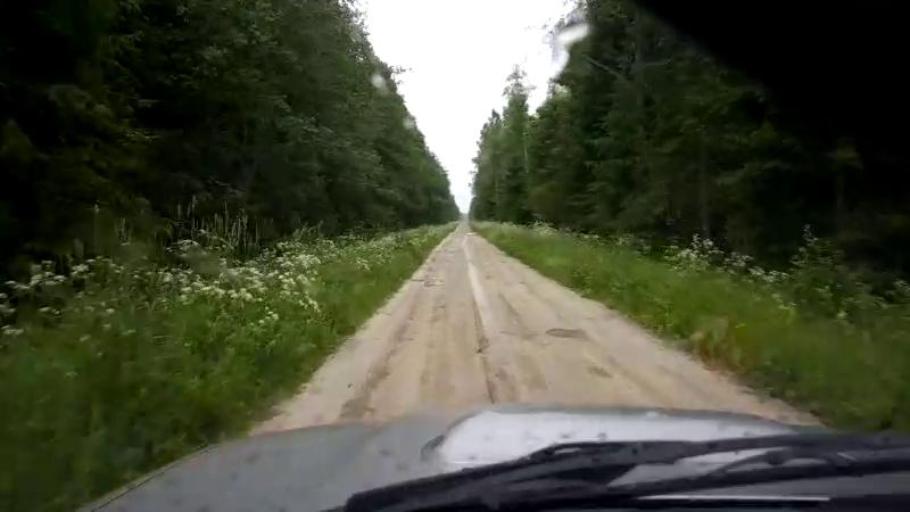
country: EE
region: Paernumaa
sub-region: Halinga vald
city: Parnu-Jaagupi
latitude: 58.5834
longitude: 24.6368
